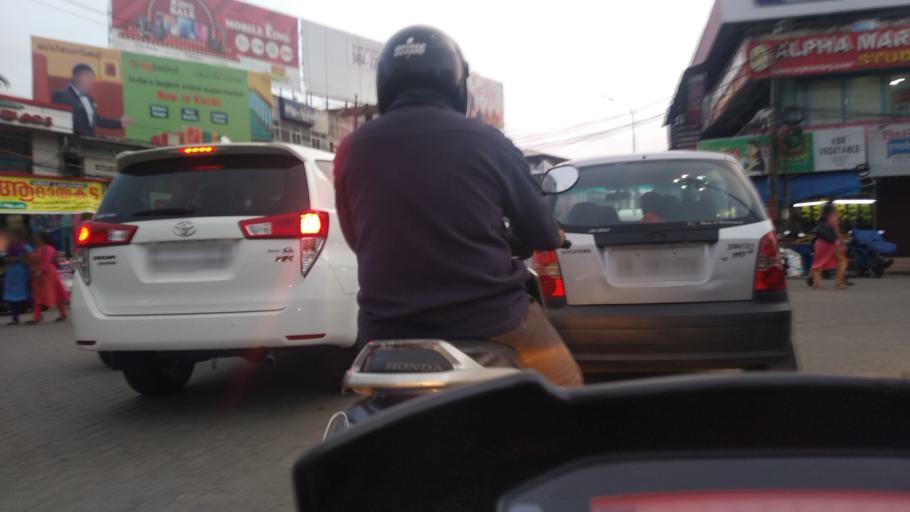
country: IN
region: Kerala
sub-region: Ernakulam
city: Elur
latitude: 10.0025
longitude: 76.3062
